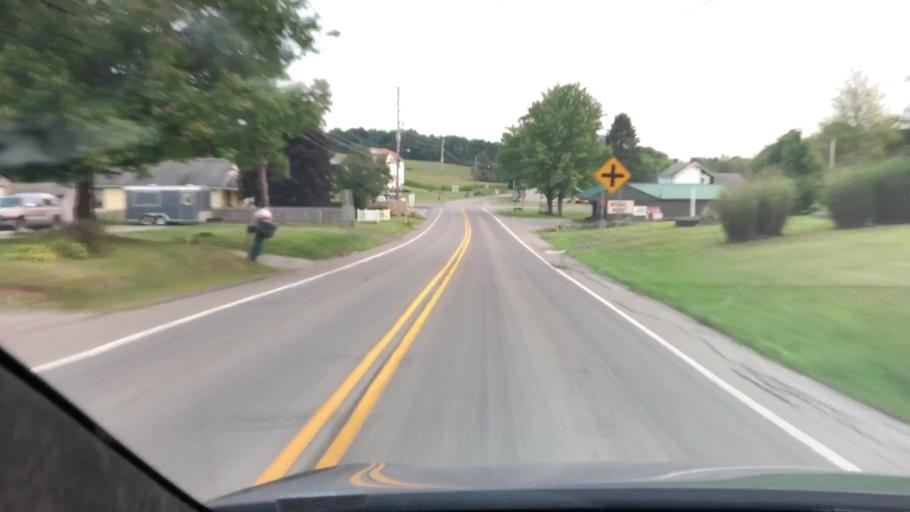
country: US
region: Pennsylvania
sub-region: Mercer County
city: Grove City
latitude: 41.1900
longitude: -79.9760
